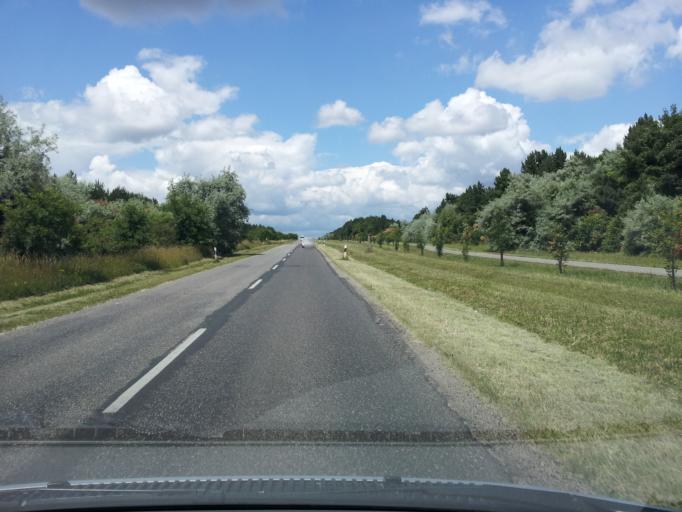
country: HU
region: Veszprem
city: Szentkiralyszabadja
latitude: 47.0635
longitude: 17.9574
